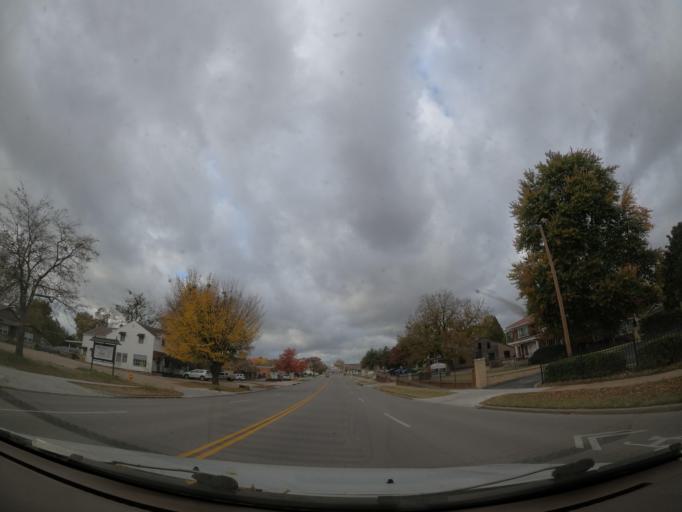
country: US
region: Oklahoma
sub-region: Tulsa County
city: Tulsa
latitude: 36.1405
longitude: -95.9628
